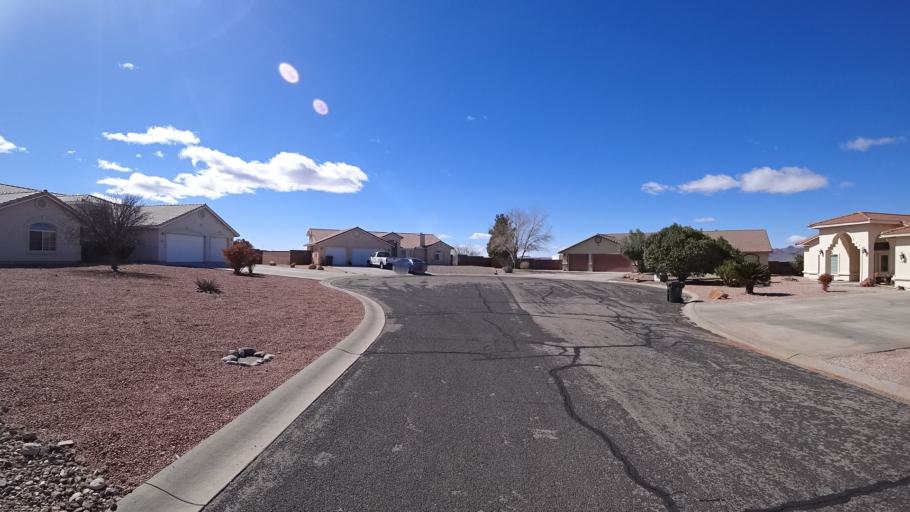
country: US
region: Arizona
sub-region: Mohave County
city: Kingman
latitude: 35.2062
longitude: -113.9753
